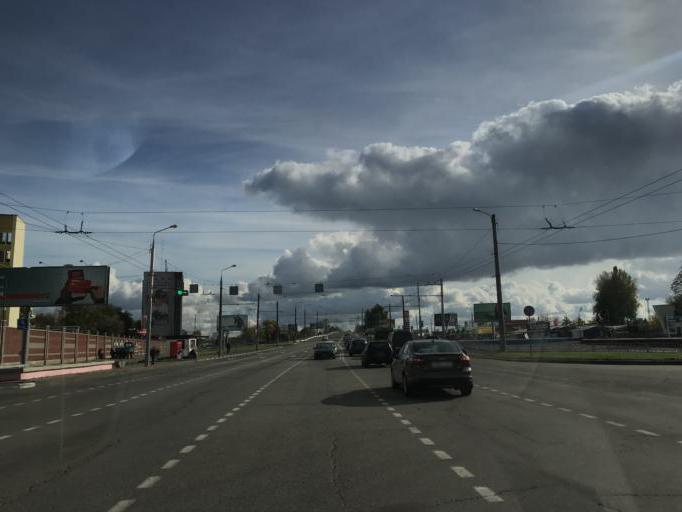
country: BY
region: Gomel
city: Gomel
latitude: 52.4475
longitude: 30.9705
